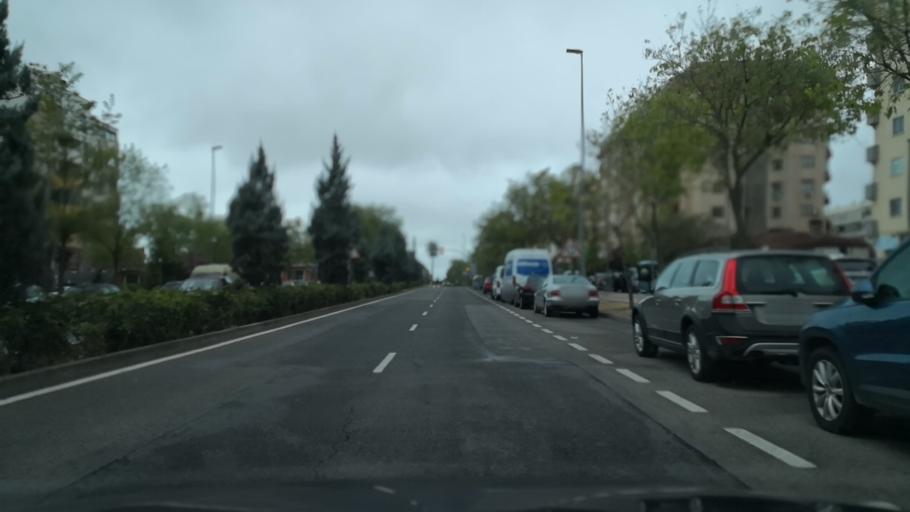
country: ES
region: Extremadura
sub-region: Provincia de Caceres
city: Caceres
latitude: 39.4704
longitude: -6.3858
